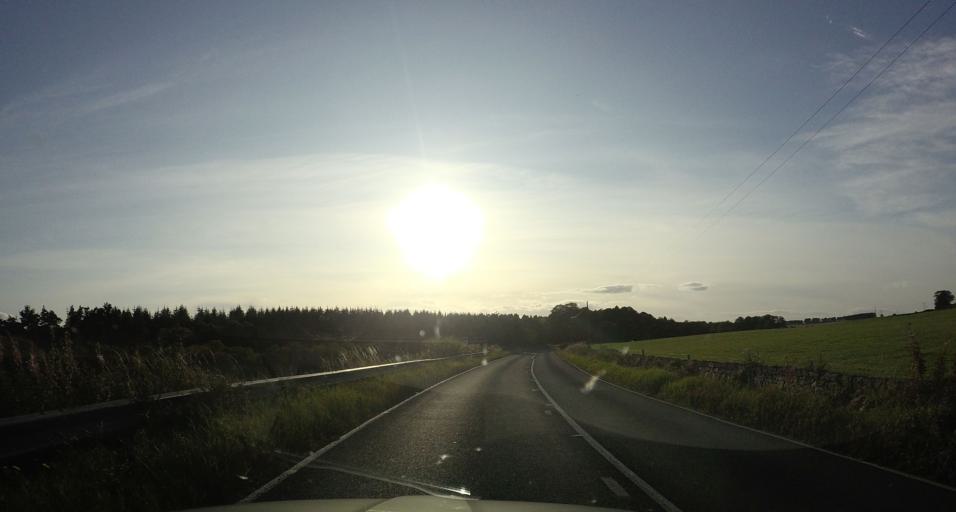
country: GB
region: Scotland
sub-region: Aberdeenshire
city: Kintore
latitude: 57.1641
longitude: -2.3694
